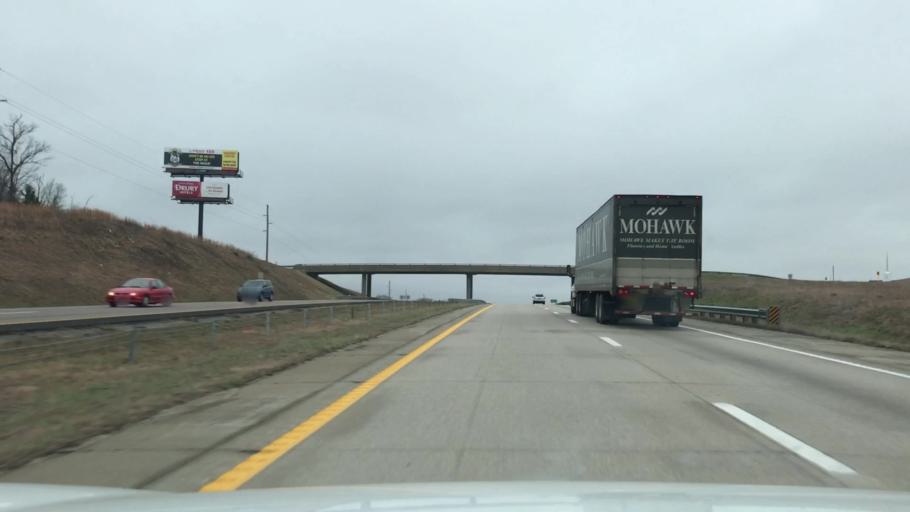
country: US
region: Missouri
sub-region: Franklin County
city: Sullivan
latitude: 38.1855
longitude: -91.1982
